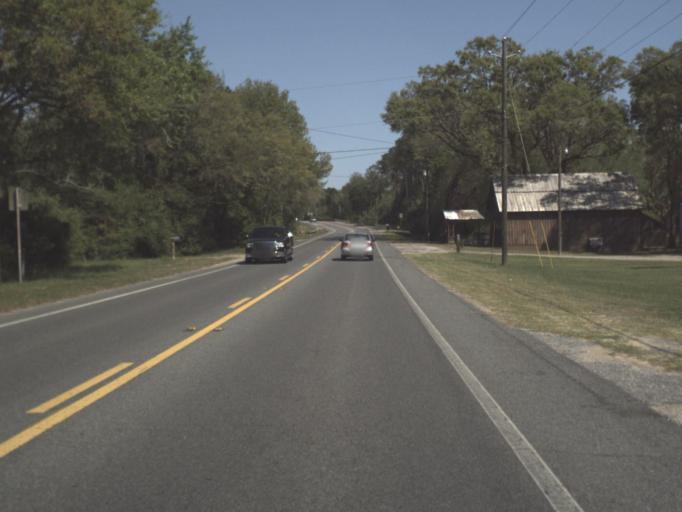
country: US
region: Florida
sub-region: Escambia County
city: Bellview
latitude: 30.4994
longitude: -87.3398
